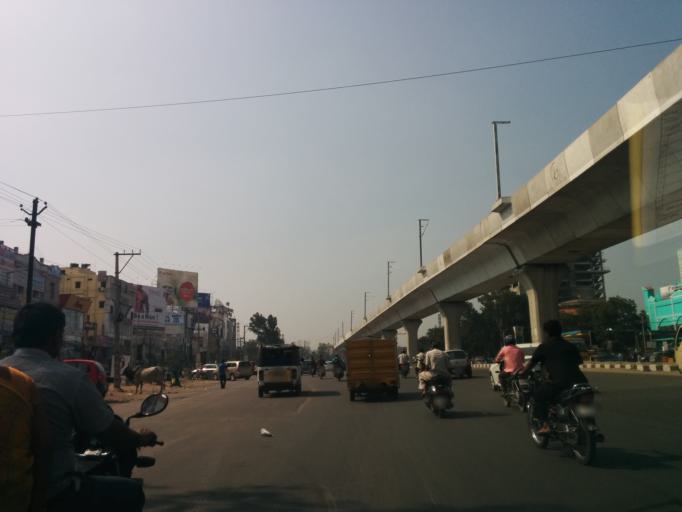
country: IN
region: Telangana
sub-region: Rangareddi
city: Kukatpalli
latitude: 17.4956
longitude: 78.3974
